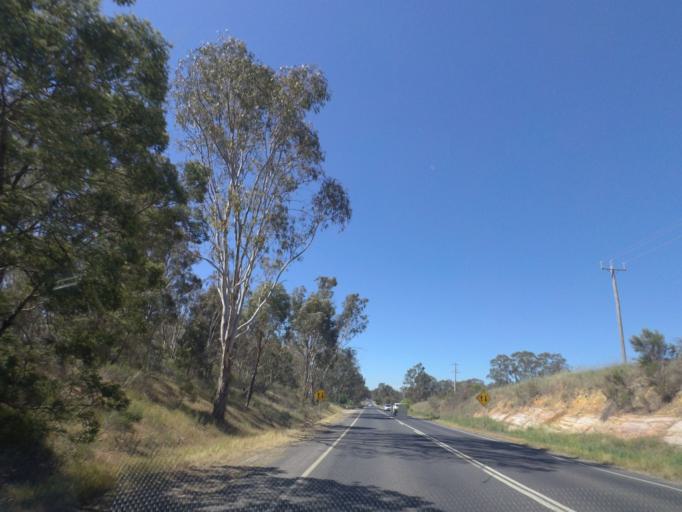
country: AU
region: Victoria
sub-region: Murrindindi
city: Kinglake West
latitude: -37.0287
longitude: 145.1066
